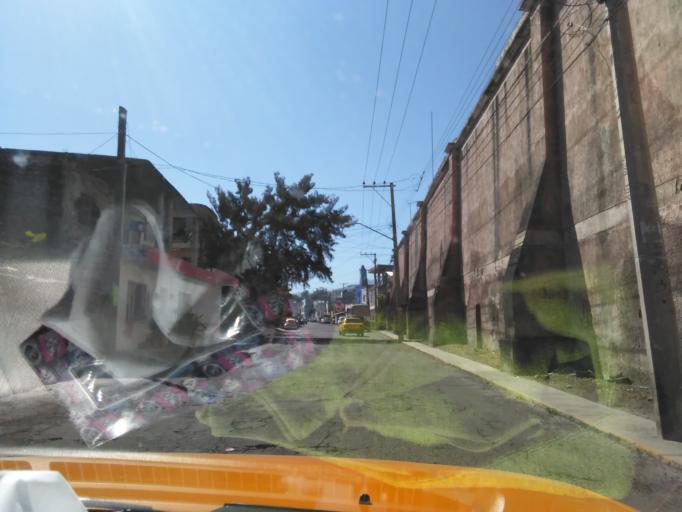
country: MX
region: Nayarit
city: Tepic
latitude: 21.5003
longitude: -104.8914
